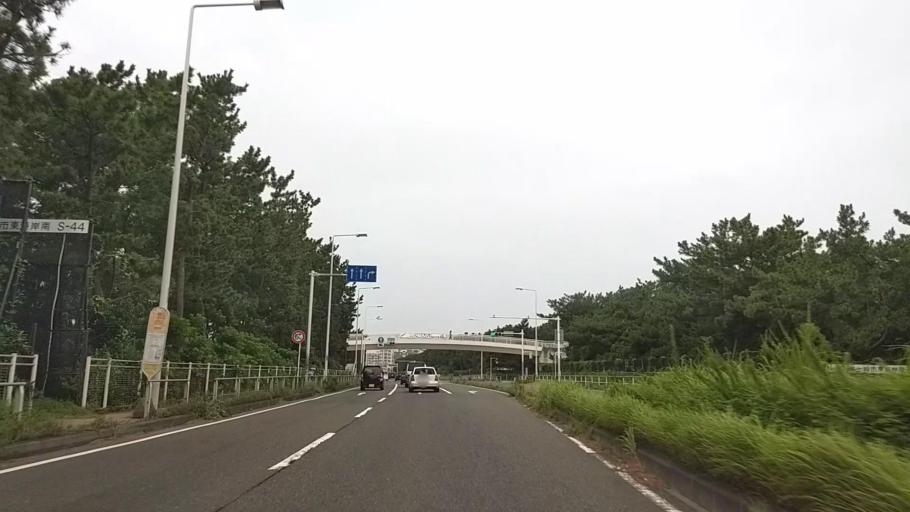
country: JP
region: Kanagawa
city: Chigasaki
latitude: 35.3186
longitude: 139.4075
